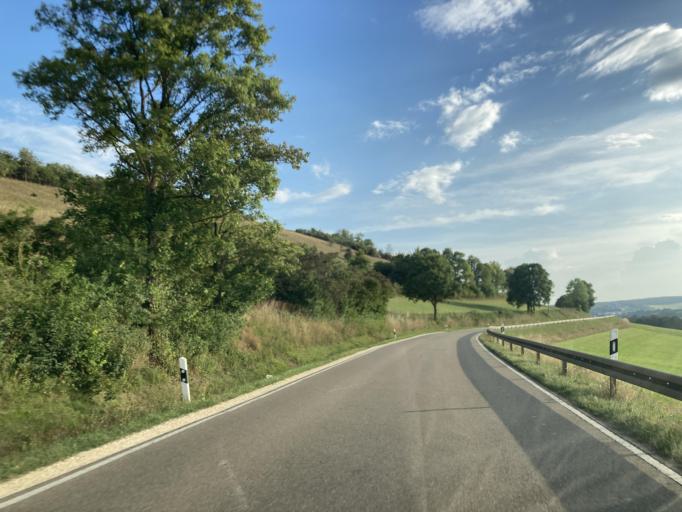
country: DE
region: Baden-Wuerttemberg
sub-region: Regierungsbezirk Stuttgart
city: Dischingen
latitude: 48.7215
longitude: 10.3863
